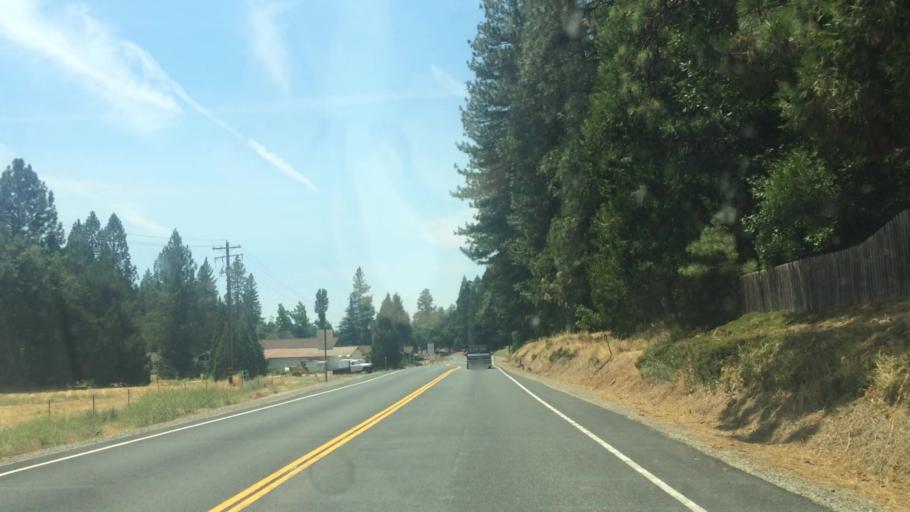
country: US
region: California
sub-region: Amador County
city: Pioneer
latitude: 38.4299
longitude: -120.5789
